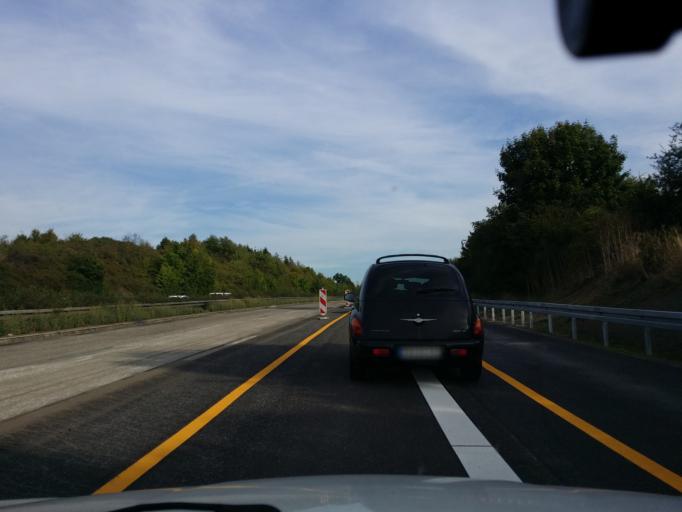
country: DE
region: Hesse
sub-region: Regierungsbezirk Giessen
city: Runkel
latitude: 50.3546
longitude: 8.1581
